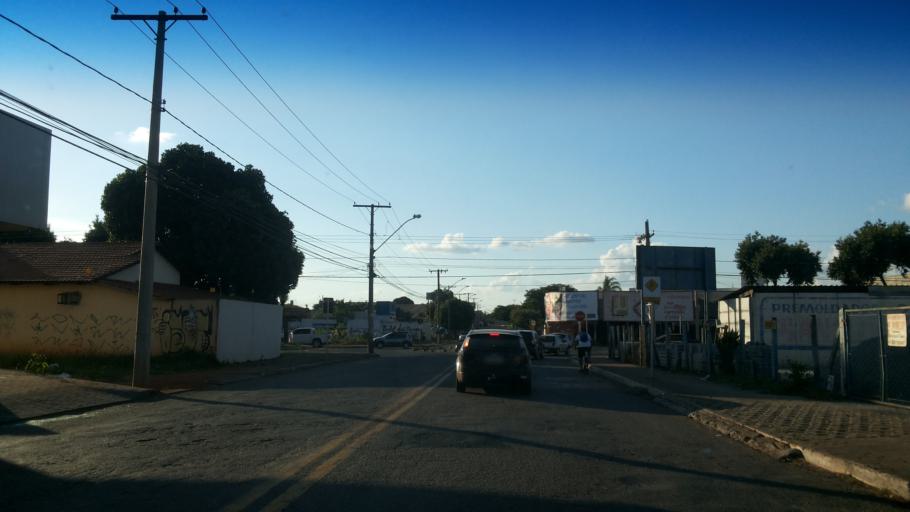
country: BR
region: Goias
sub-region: Goiania
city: Goiania
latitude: -16.7166
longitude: -49.3067
